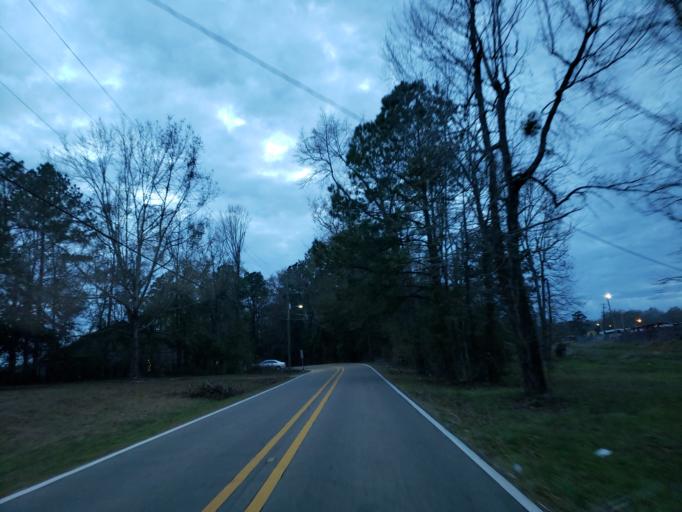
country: US
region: Mississippi
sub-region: Forrest County
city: Petal
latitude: 31.3346
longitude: -89.2597
